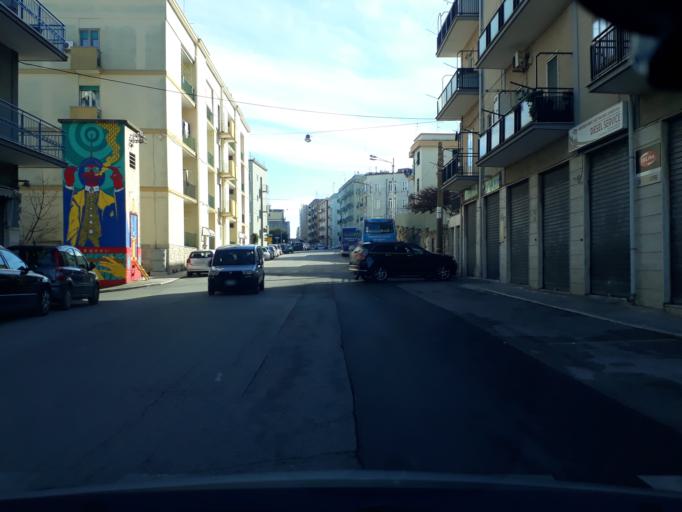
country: IT
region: Apulia
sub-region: Provincia di Taranto
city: Martina Franca
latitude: 40.7062
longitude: 17.3414
